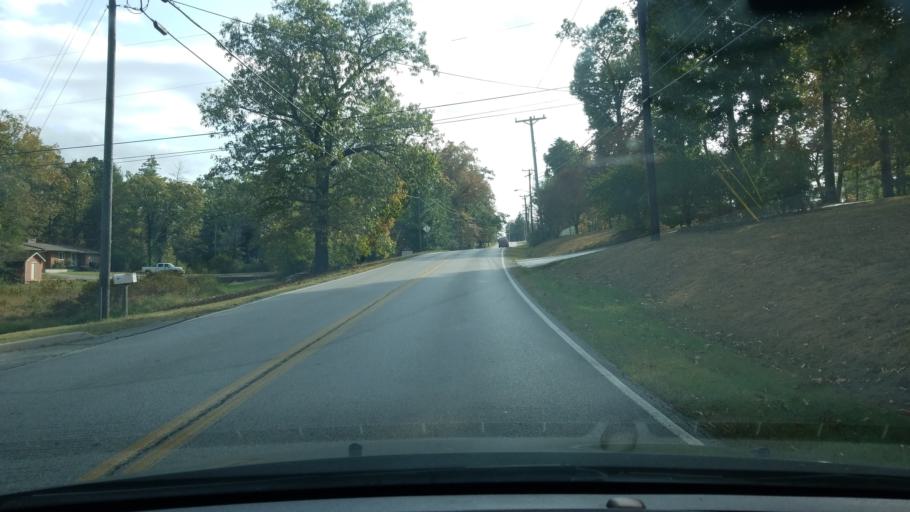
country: US
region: Tennessee
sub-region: Cumberland County
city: Crossville
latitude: 35.9742
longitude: -85.0350
